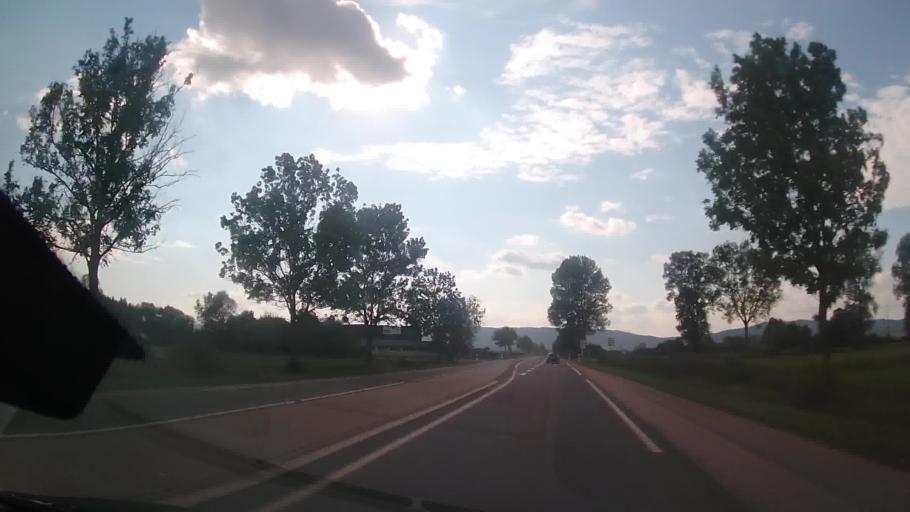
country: FR
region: Franche-Comte
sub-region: Departement du Jura
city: Clairvaux-les-Lacs
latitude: 46.5894
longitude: 5.7208
